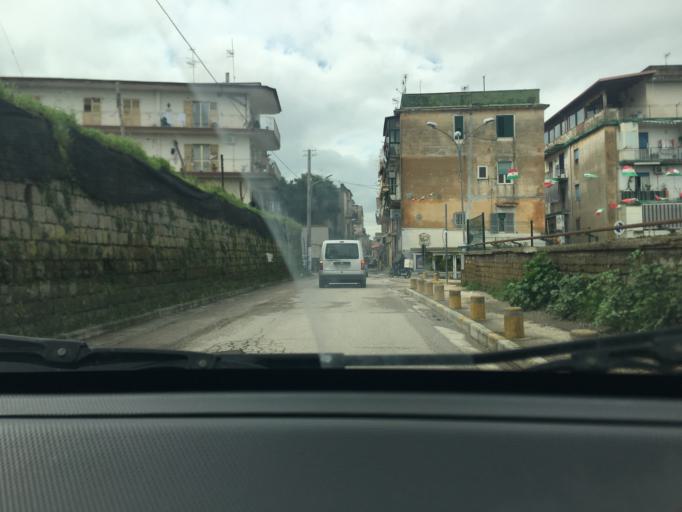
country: IT
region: Campania
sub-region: Provincia di Napoli
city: Calvizzano
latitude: 40.8956
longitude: 14.1958
